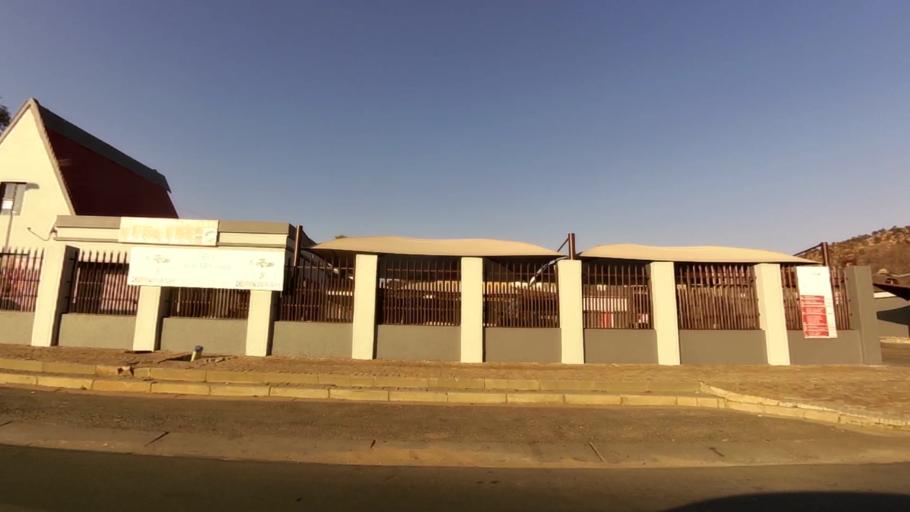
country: ZA
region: Gauteng
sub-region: City of Johannesburg Metropolitan Municipality
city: Soweto
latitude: -26.2764
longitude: 27.9626
